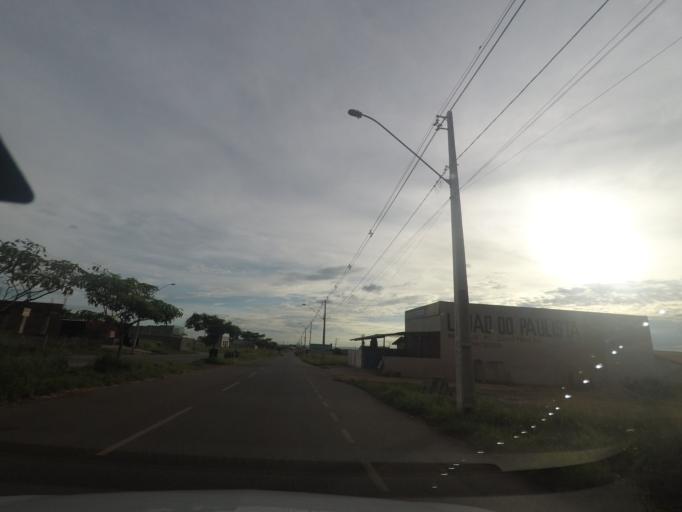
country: BR
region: Goias
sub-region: Trindade
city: Trindade
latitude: -16.7248
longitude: -49.4042
